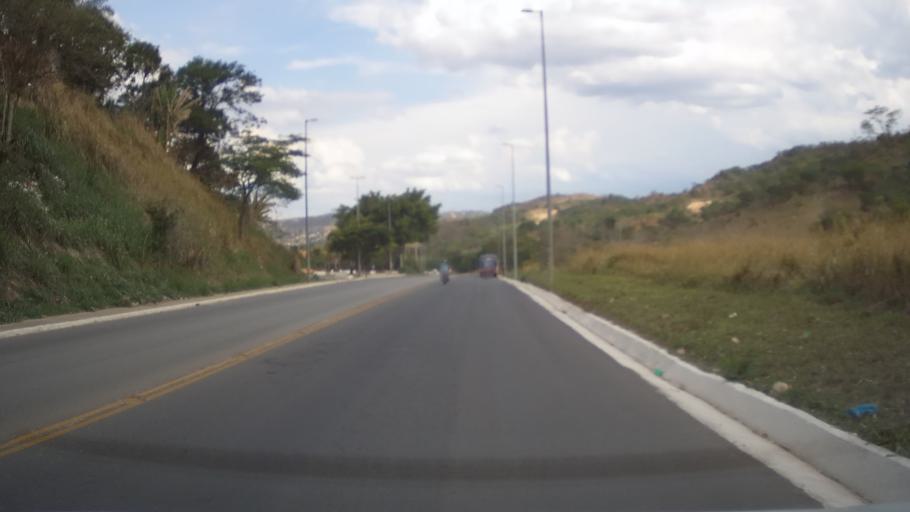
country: BR
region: Minas Gerais
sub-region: Belo Horizonte
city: Belo Horizonte
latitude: -19.8692
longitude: -43.8916
